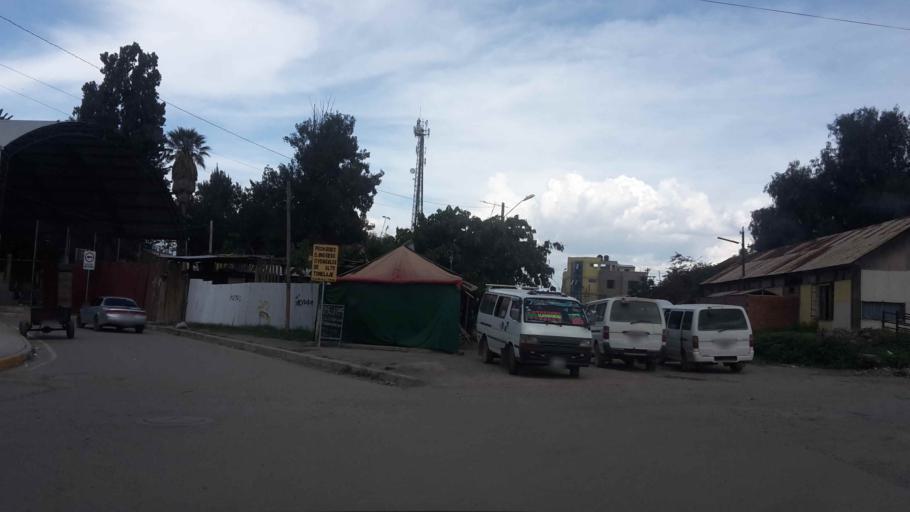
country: BO
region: Cochabamba
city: Sipe Sipe
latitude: -17.4021
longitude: -66.2827
